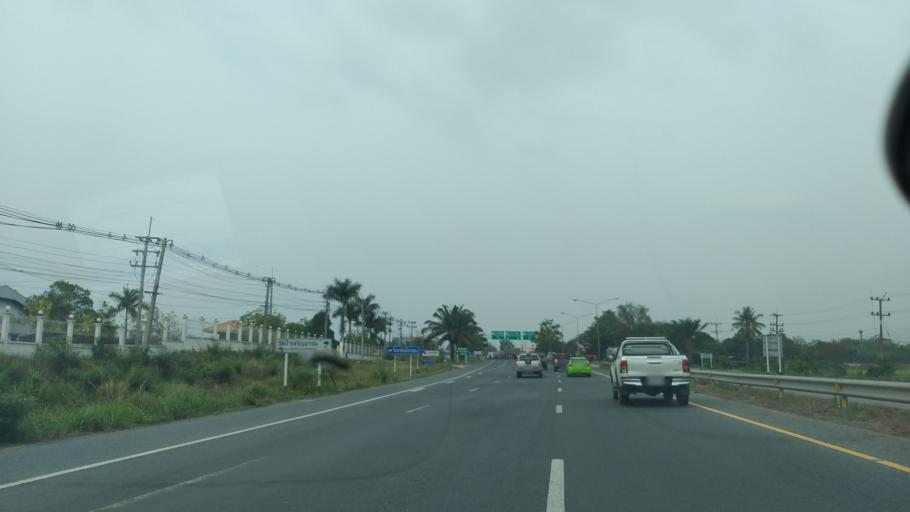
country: TH
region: Chon Buri
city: Ko Chan
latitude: 13.3208
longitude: 101.2692
